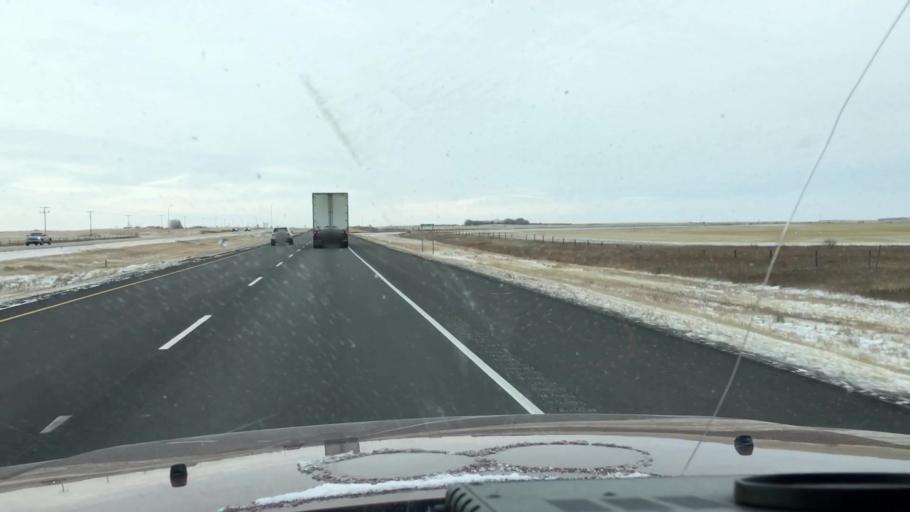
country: CA
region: Saskatchewan
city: Saskatoon
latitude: 51.7969
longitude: -106.4875
